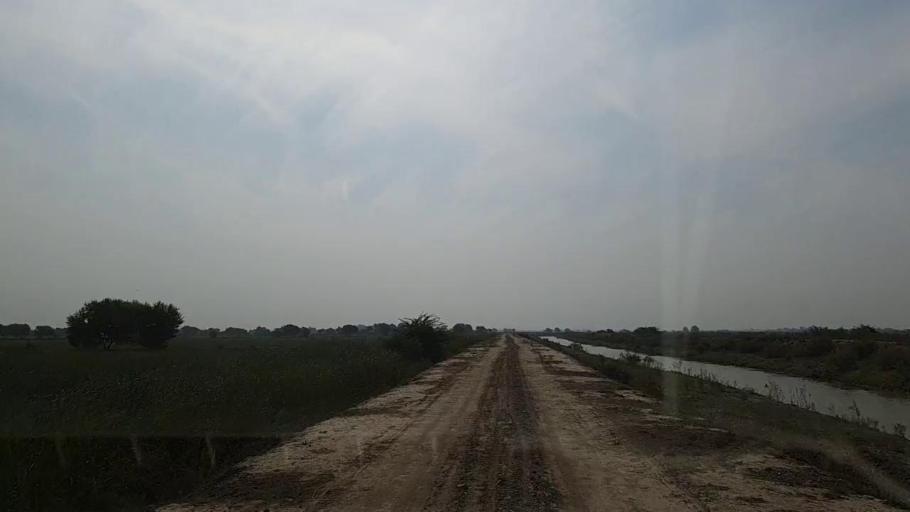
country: PK
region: Sindh
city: Mirpur Batoro
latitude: 24.6663
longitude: 68.2503
